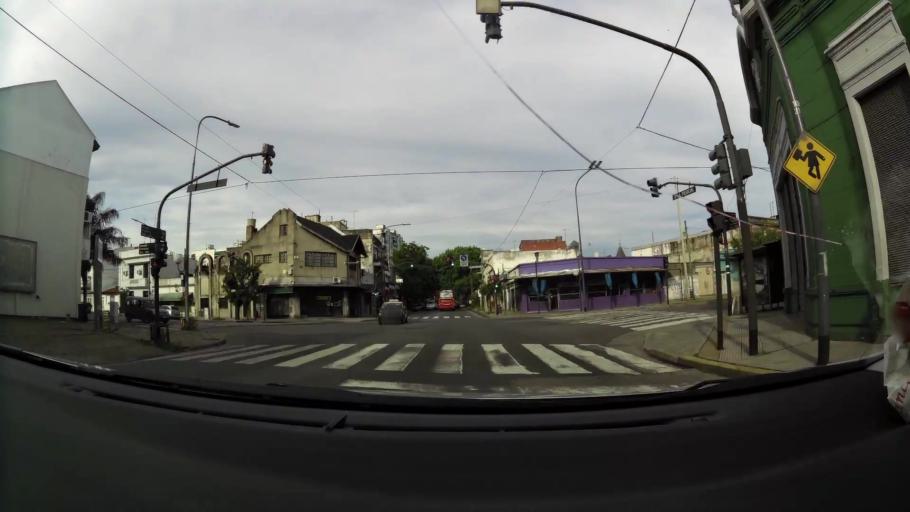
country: AR
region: Buenos Aires F.D.
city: Villa Santa Rita
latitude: -34.6376
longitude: -58.4516
